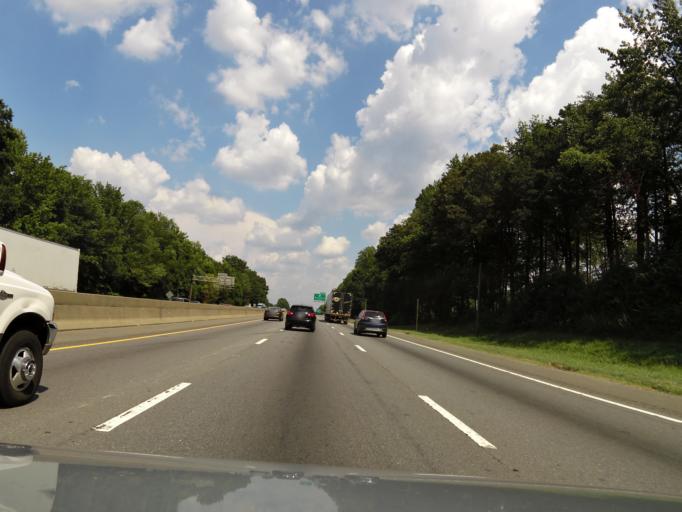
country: US
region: North Carolina
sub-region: Gaston County
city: Lowell
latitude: 35.2613
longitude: -81.0972
